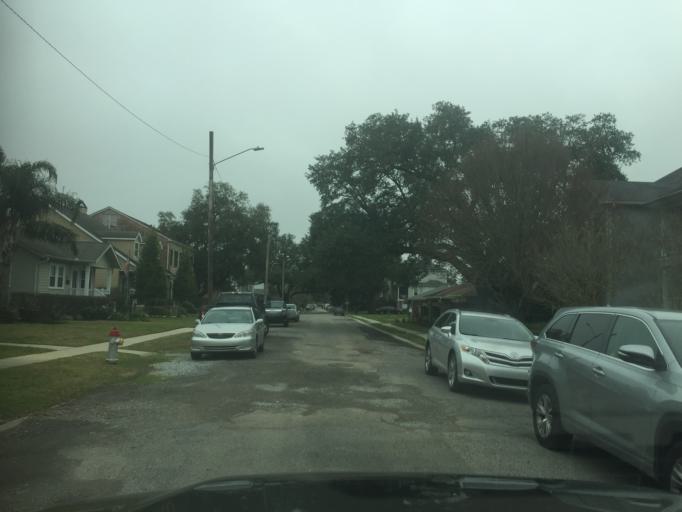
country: US
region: Louisiana
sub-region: Jefferson Parish
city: Metairie
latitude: 30.0133
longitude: -90.1104
